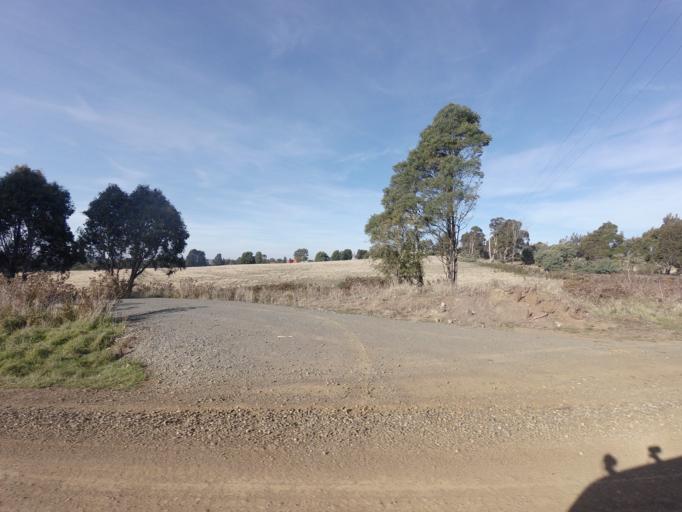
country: AU
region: Tasmania
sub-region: Brighton
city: Bridgewater
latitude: -42.4854
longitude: 147.3870
